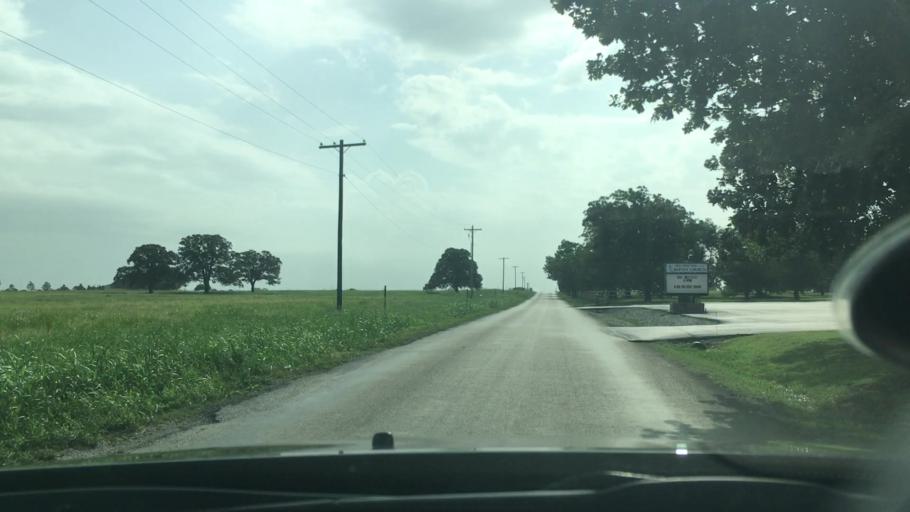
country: US
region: Oklahoma
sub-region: Carter County
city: Lone Grove
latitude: 34.2020
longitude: -97.2638
